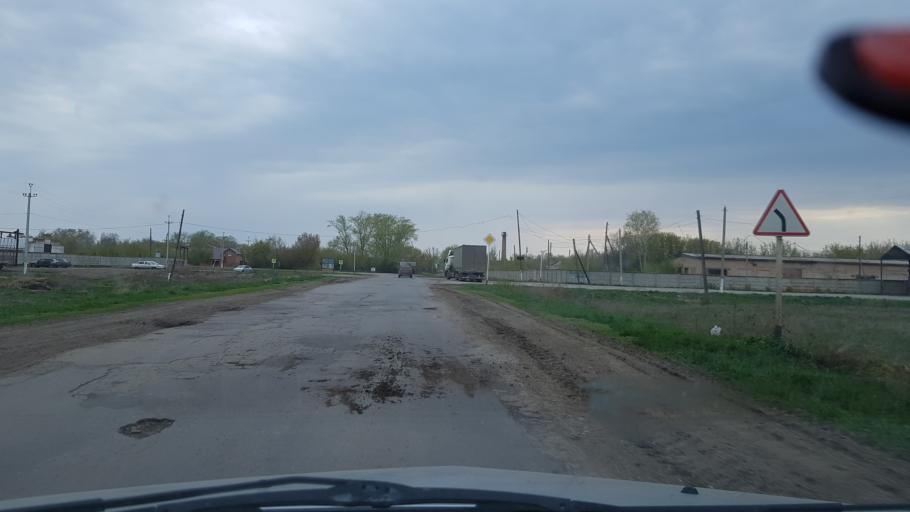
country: RU
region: Samara
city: Khryashchevka
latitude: 53.6728
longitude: 49.0806
